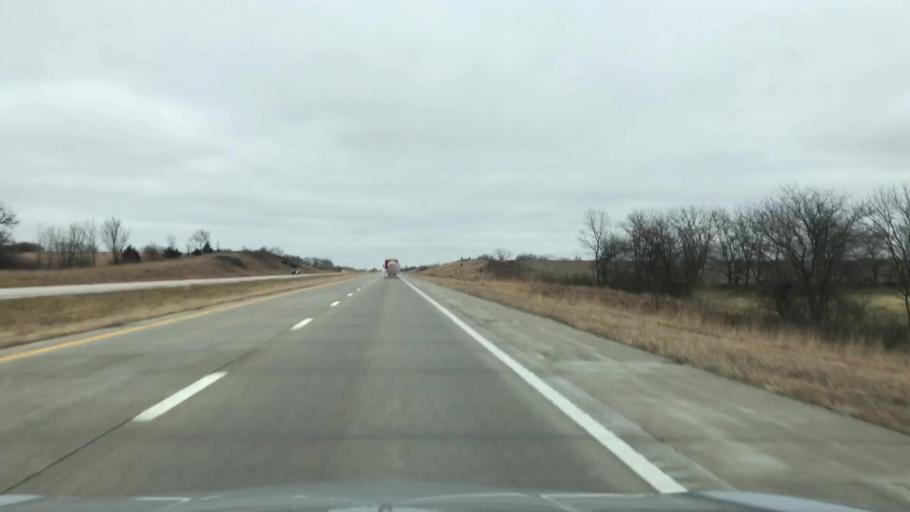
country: US
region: Missouri
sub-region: Caldwell County
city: Hamilton
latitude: 39.7345
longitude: -93.9608
